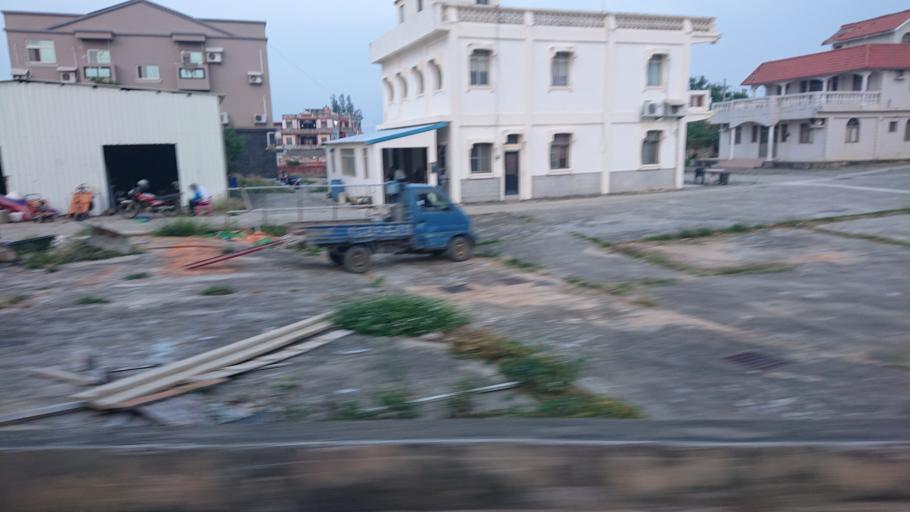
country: TW
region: Fukien
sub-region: Kinmen
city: Jincheng
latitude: 24.4617
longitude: 118.3239
